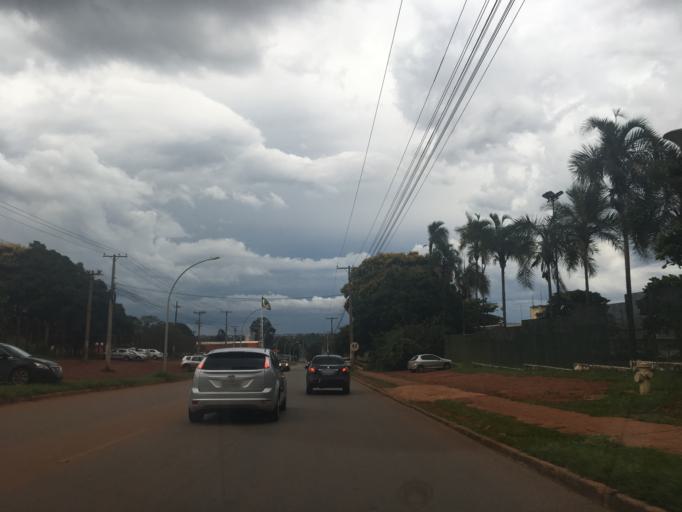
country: BR
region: Federal District
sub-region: Brasilia
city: Brasilia
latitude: -15.7379
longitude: -47.9027
